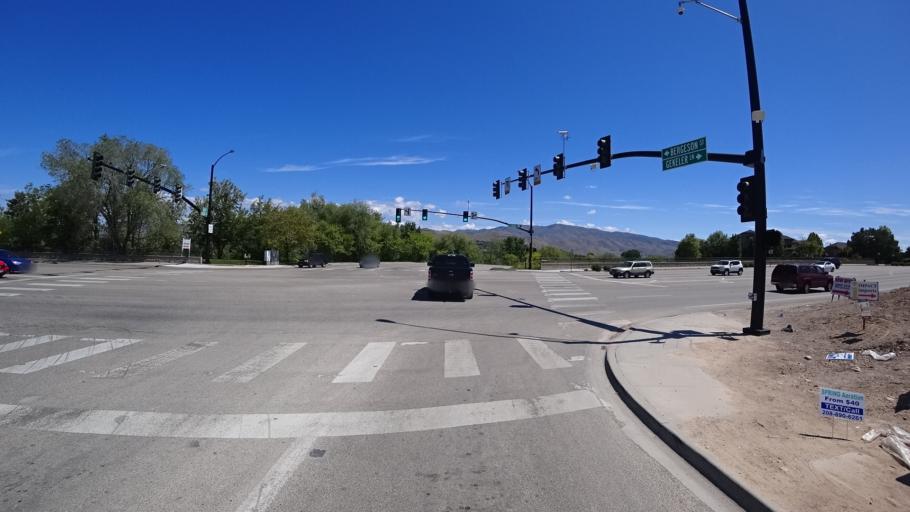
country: US
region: Idaho
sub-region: Ada County
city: Boise
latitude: 43.5680
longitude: -116.1825
